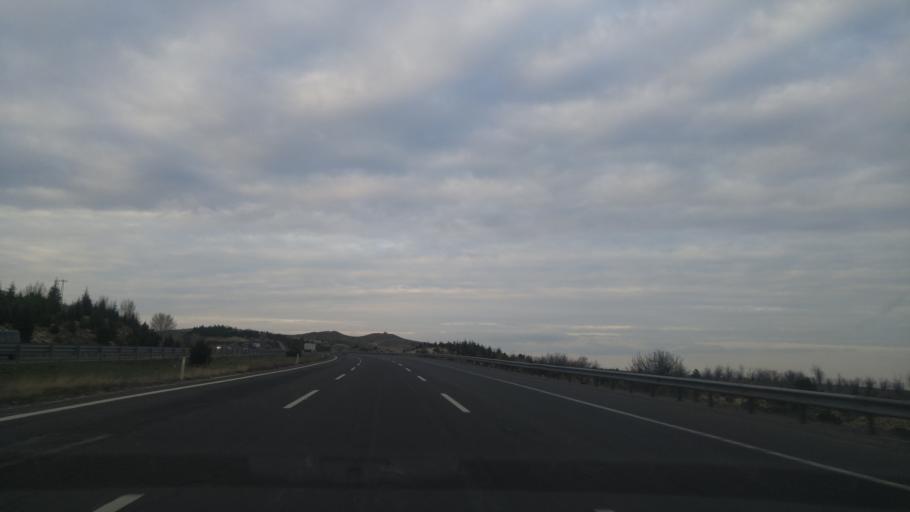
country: TR
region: Ankara
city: Kazan
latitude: 40.1886
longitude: 32.5908
